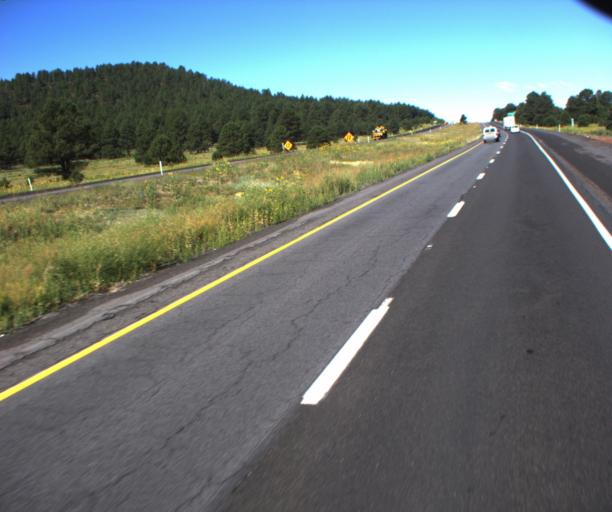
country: US
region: Arizona
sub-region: Coconino County
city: Williams
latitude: 35.2586
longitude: -112.0949
